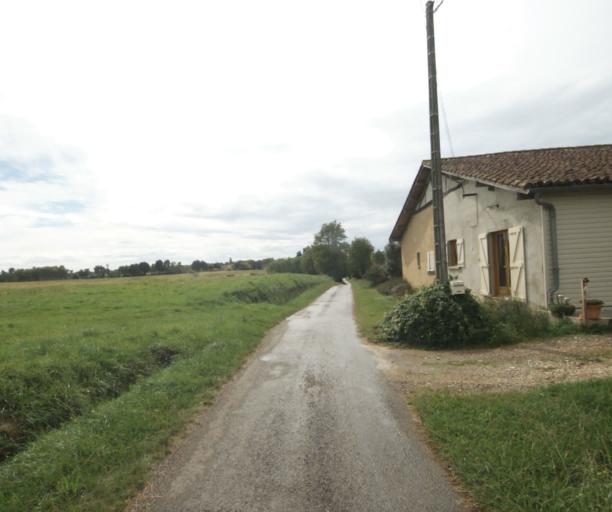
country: FR
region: Midi-Pyrenees
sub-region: Departement du Gers
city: Cazaubon
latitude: 43.9095
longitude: -0.1190
